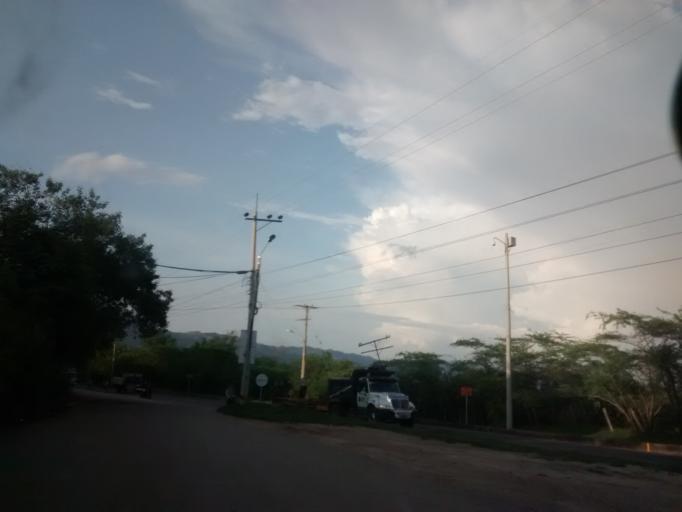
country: CO
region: Cundinamarca
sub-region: Girardot
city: Girardot City
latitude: 4.3265
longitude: -74.8037
